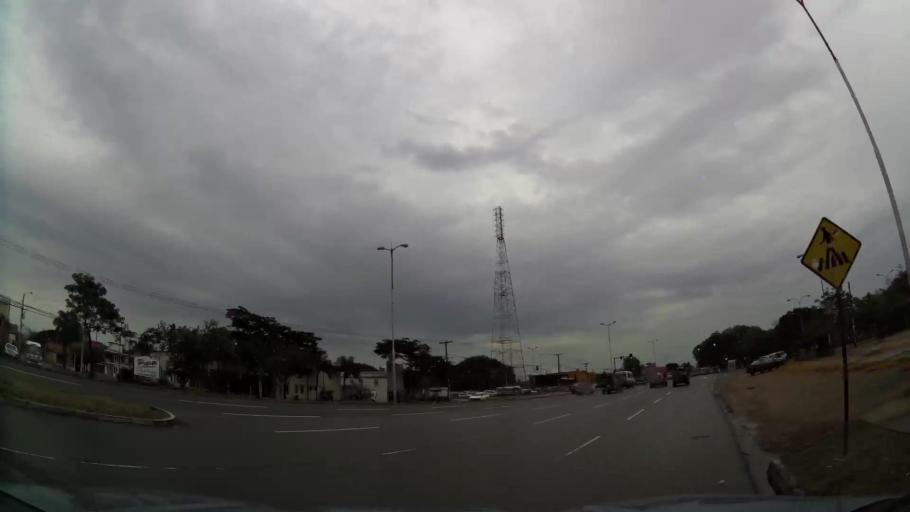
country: BO
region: Santa Cruz
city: Santa Cruz de la Sierra
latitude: -17.7938
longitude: -63.1663
